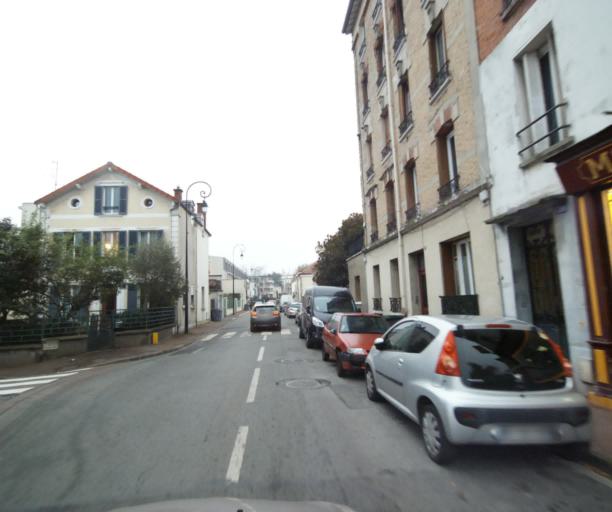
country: FR
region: Ile-de-France
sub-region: Departement de Seine-Saint-Denis
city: Neuilly-Plaisance
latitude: 48.8605
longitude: 2.5114
